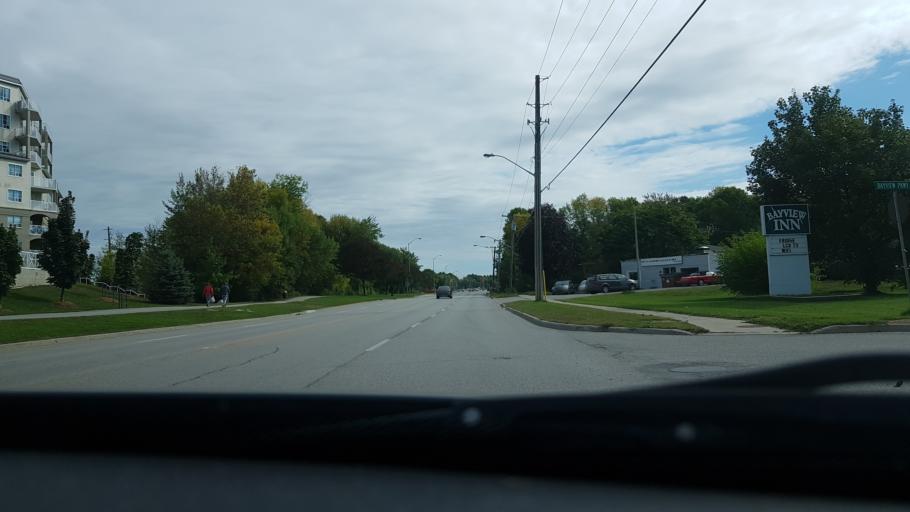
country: CA
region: Ontario
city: Orillia
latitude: 44.6059
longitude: -79.3929
